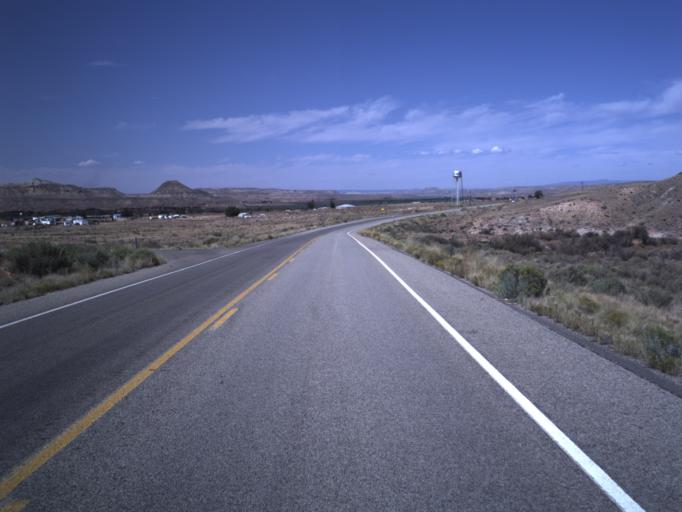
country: US
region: Colorado
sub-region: Montezuma County
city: Towaoc
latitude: 37.1944
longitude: -109.1435
